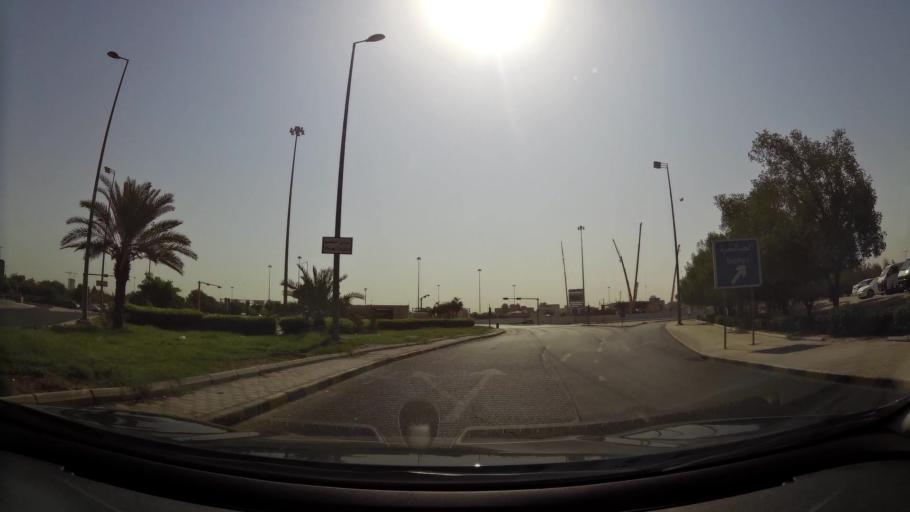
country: KW
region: Al Asimah
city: Kuwait City
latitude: 29.3669
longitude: 47.9894
